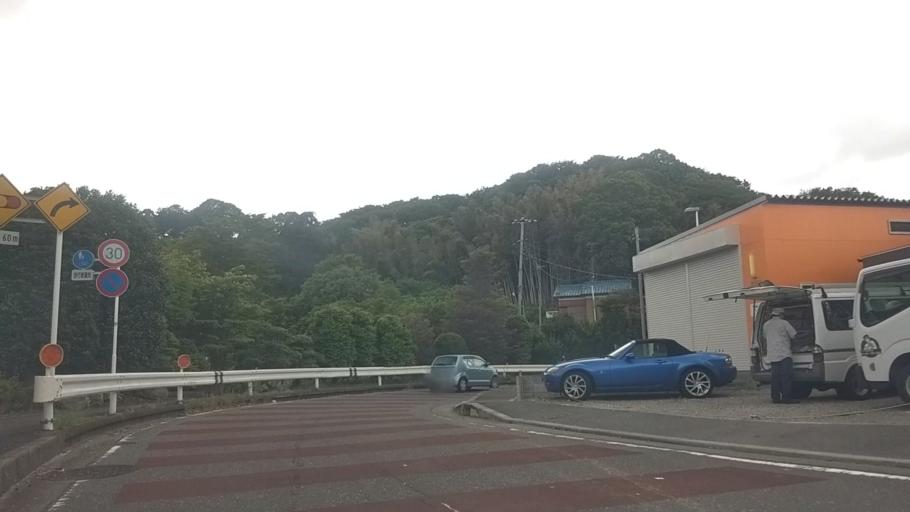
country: JP
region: Kanagawa
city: Fujisawa
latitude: 35.3582
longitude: 139.5108
